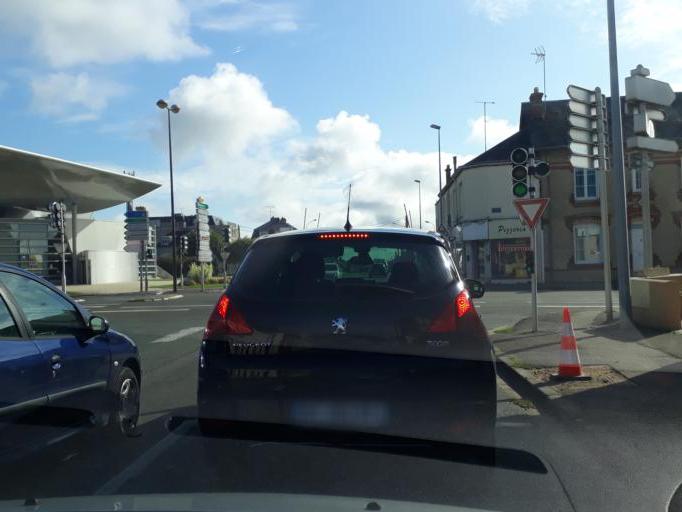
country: FR
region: Centre
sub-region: Departement d'Eure-et-Loir
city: Chateaudun
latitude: 48.0712
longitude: 1.3370
